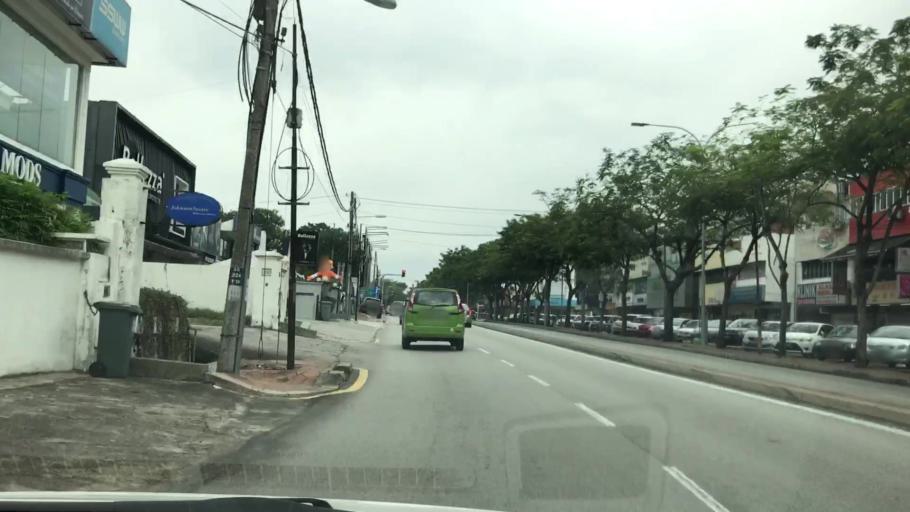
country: MY
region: Selangor
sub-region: Petaling
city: Petaling Jaya
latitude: 3.1169
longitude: 101.6232
